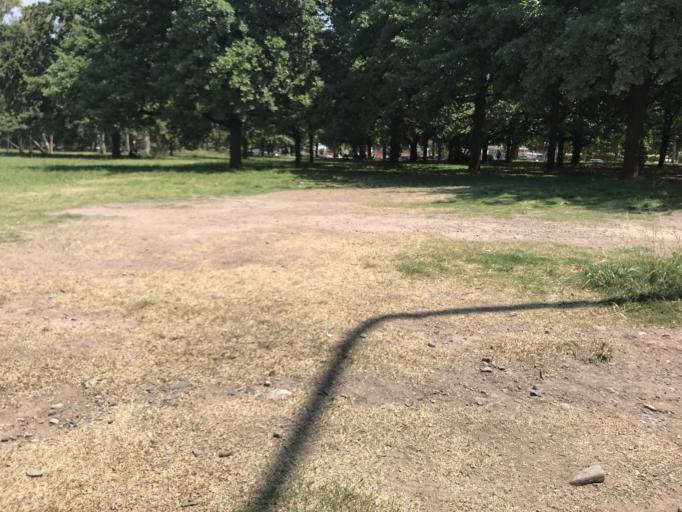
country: AR
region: Mendoza
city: Mendoza
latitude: -32.8946
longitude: -68.8663
